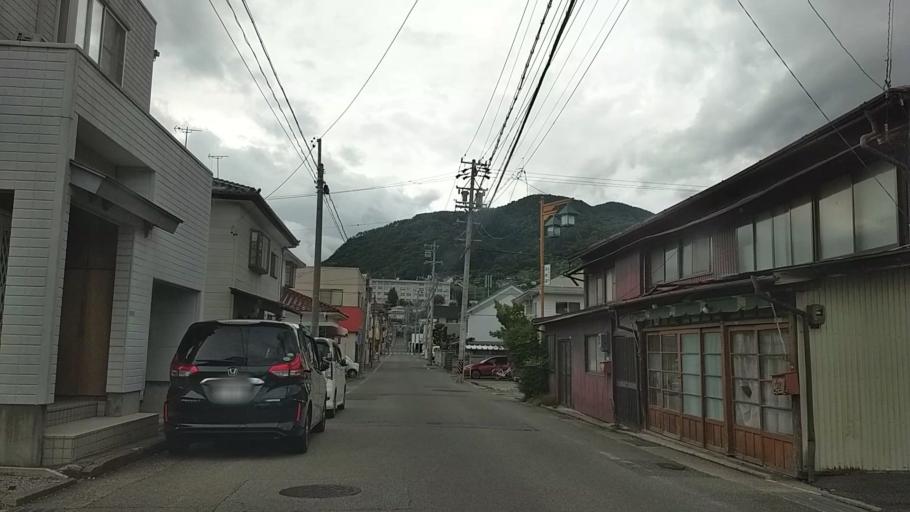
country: JP
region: Nagano
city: Nagano-shi
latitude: 36.6641
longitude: 138.1896
